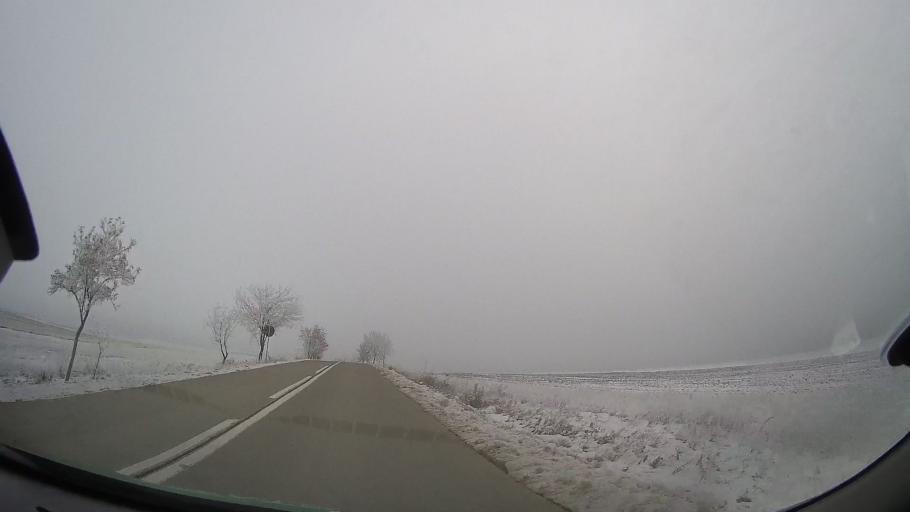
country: RO
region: Vaslui
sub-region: Comuna Ivesti
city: Ivesti
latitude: 46.1941
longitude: 27.5766
